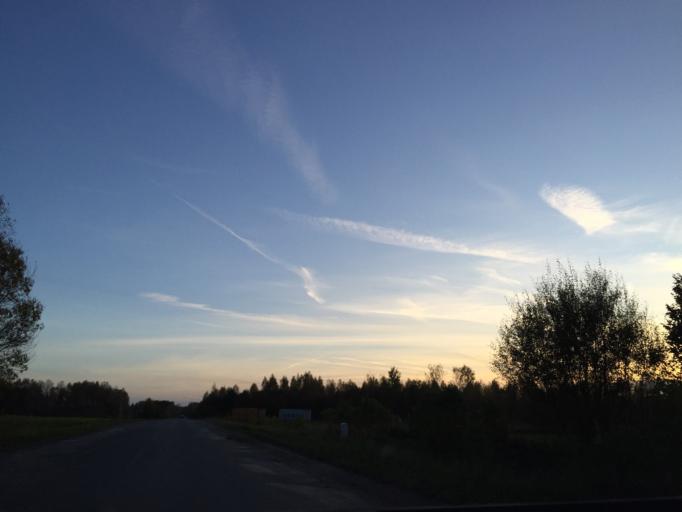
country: LV
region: Malpils
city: Malpils
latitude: 56.8931
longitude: 24.9324
